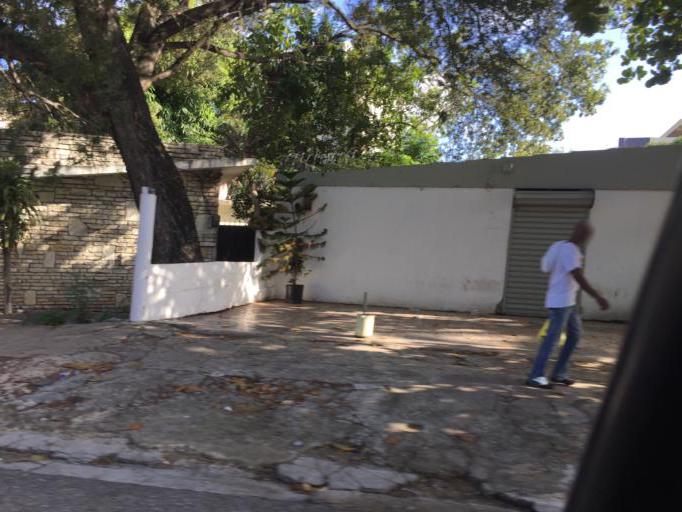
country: DO
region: Nacional
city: La Julia
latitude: 18.4619
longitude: -69.9215
